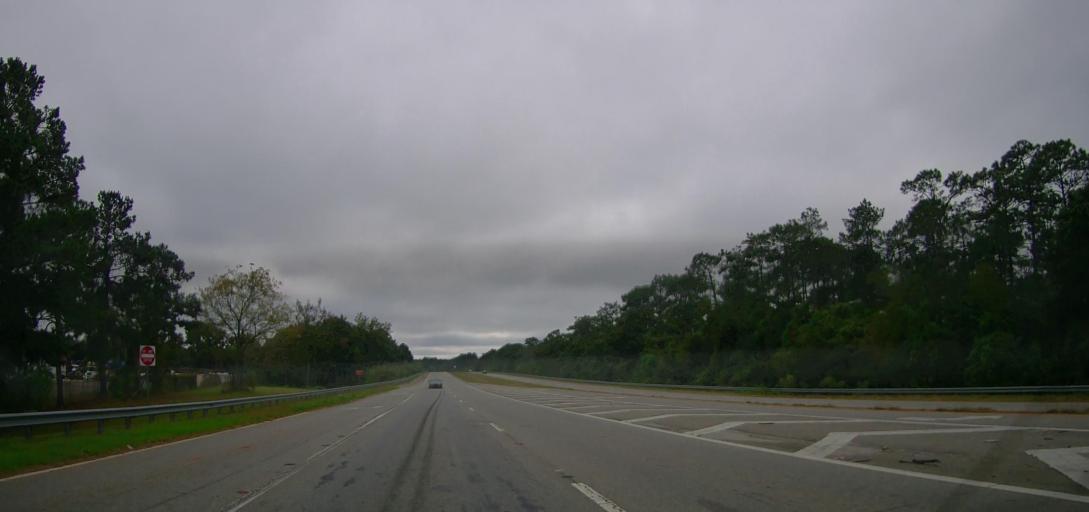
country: US
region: Georgia
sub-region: Thomas County
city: Thomasville
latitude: 30.8300
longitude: -84.0071
